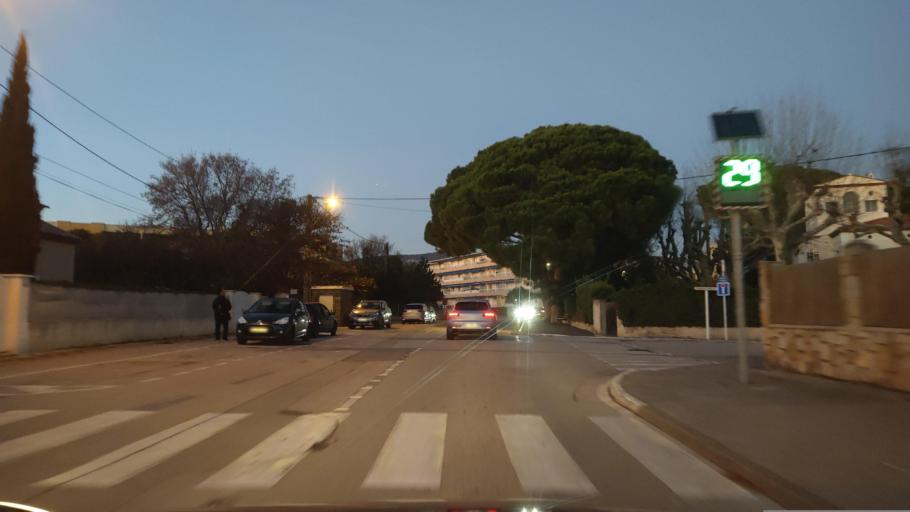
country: FR
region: Provence-Alpes-Cote d'Azur
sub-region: Departement du Var
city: Sanary-sur-Mer
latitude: 43.1172
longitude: 5.8117
